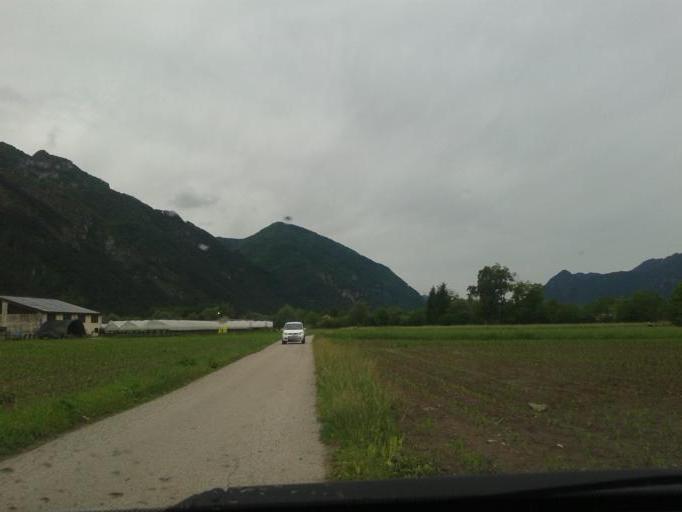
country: IT
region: Trentino-Alto Adige
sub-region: Provincia di Trento
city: Lodrone-Darzo
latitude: 45.8335
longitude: 10.5541
